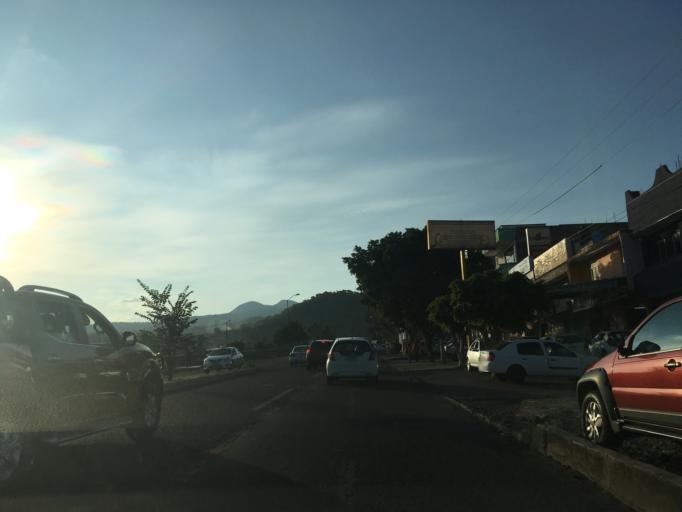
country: MX
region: Michoacan
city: Morelia
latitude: 19.7145
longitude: -101.2286
